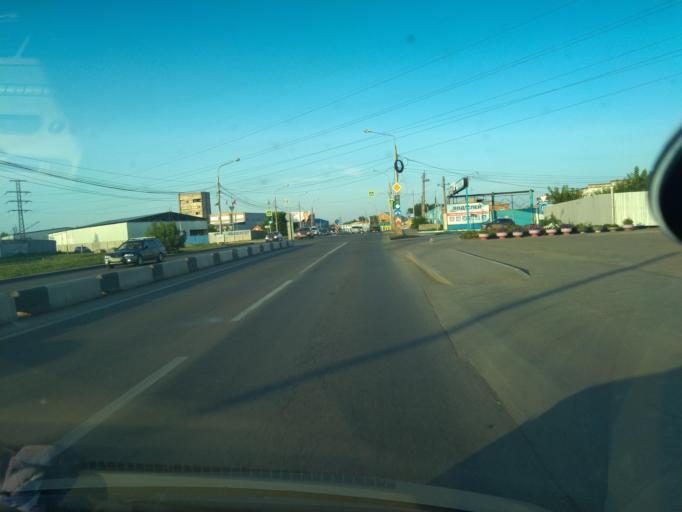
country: RU
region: Krasnoyarskiy
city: Berezovka
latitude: 56.0199
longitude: 93.0348
